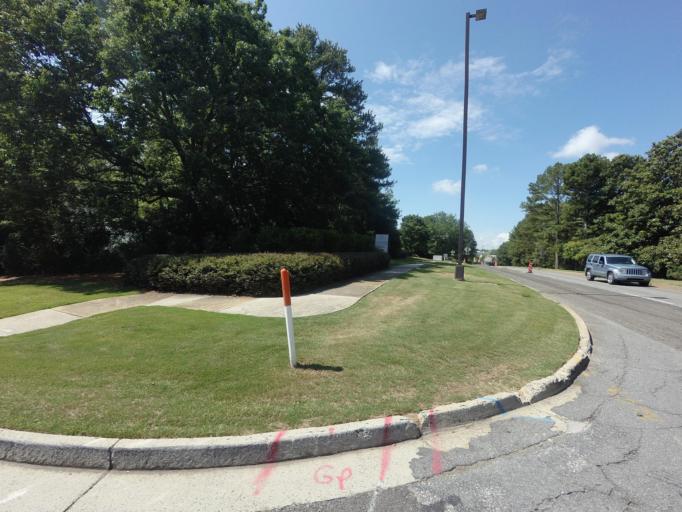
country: US
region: Georgia
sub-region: Fulton County
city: Johns Creek
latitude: 34.0576
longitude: -84.1666
